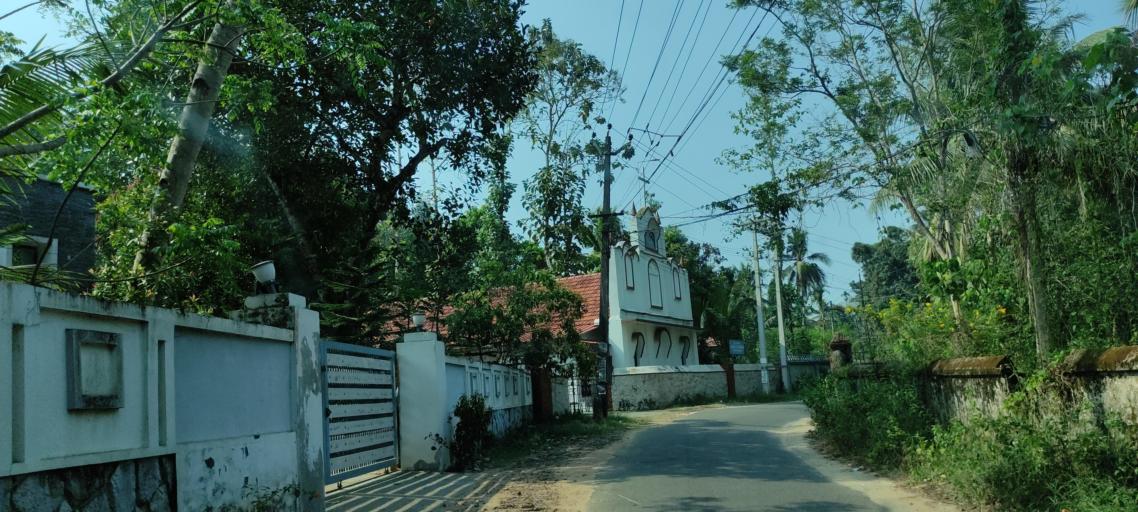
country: IN
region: Kerala
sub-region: Pattanamtitta
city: Tiruvalla
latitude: 9.3517
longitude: 76.5274
